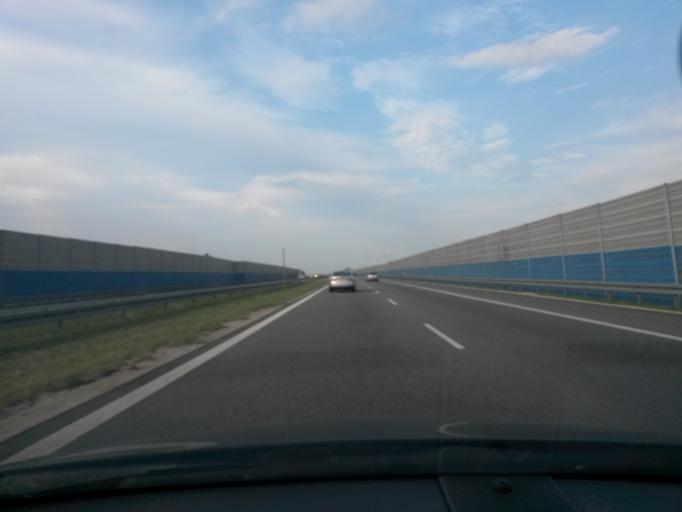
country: PL
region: Lodz Voivodeship
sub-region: Powiat brzezinski
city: Dmosin
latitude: 51.9283
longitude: 19.7912
